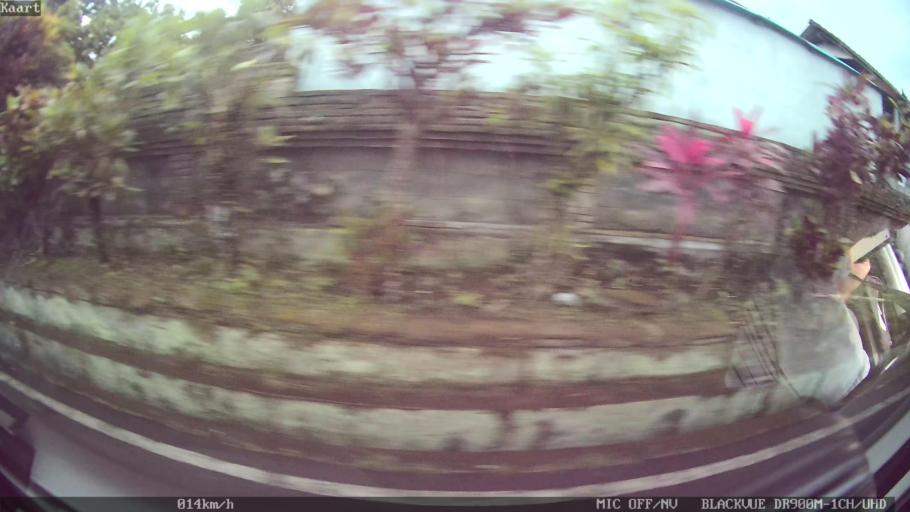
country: ID
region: Bali
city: Banjar Mambalkajanan
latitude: -8.5516
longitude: 115.2112
